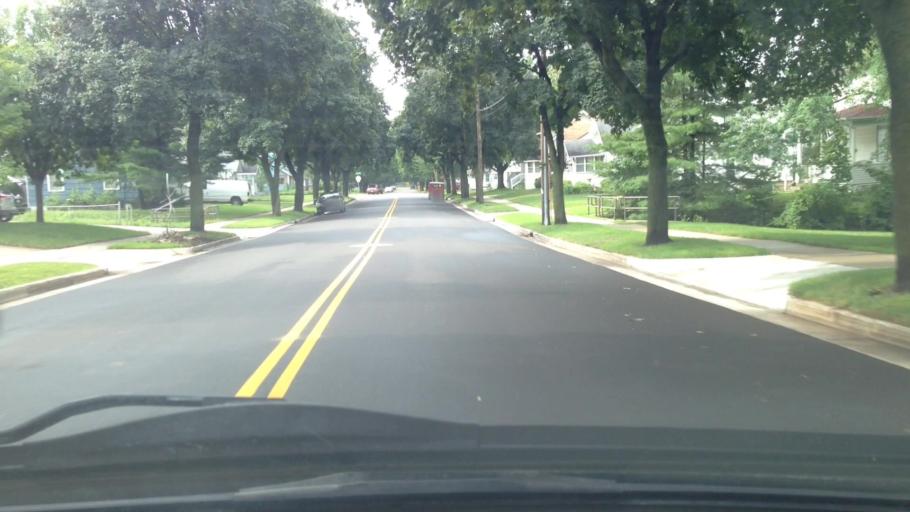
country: US
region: Minnesota
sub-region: Olmsted County
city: Rochester
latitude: 44.0183
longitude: -92.4488
